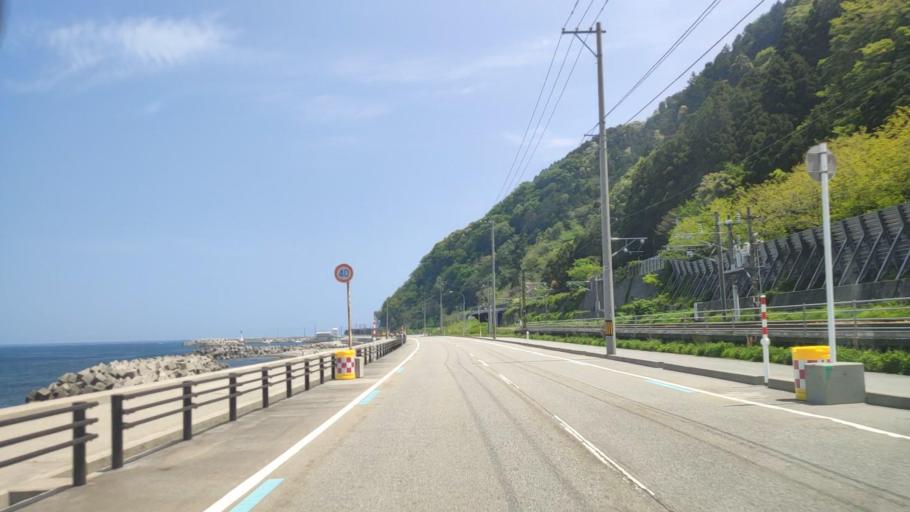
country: JP
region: Toyama
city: Nyuzen
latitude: 36.9684
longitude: 137.5808
